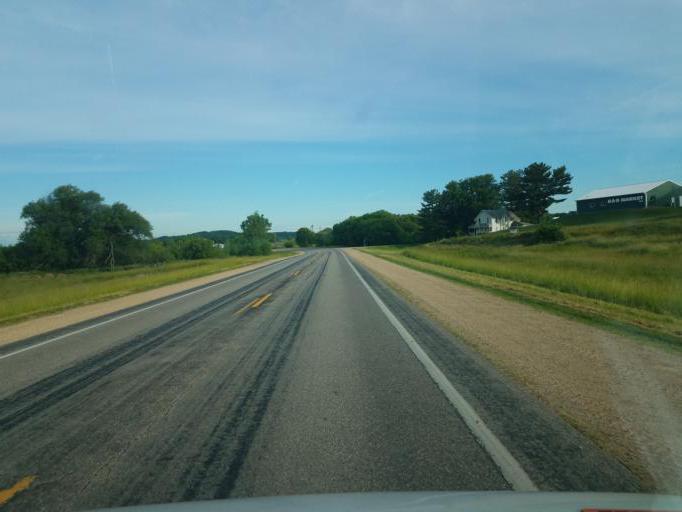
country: US
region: Wisconsin
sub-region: Vernon County
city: Hillsboro
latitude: 43.6564
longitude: -90.3660
